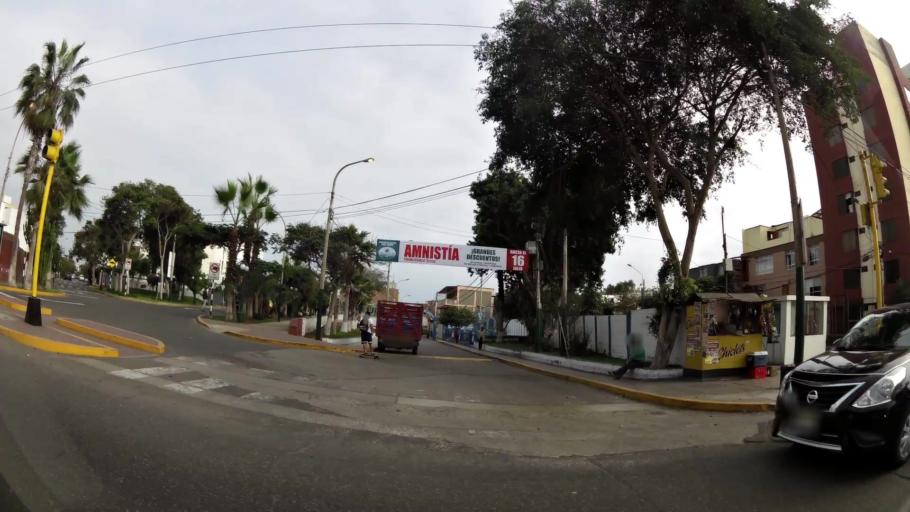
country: PE
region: Lima
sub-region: Lima
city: San Isidro
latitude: -12.1011
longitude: -77.0608
